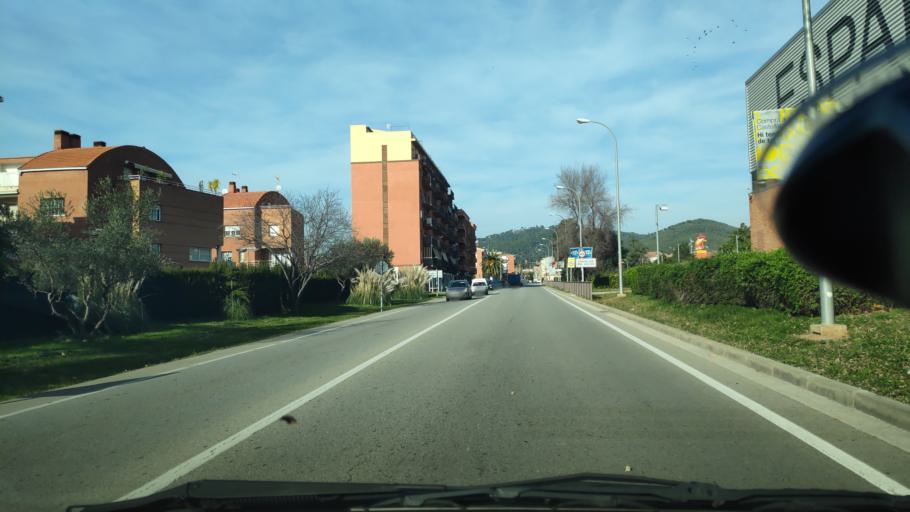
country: ES
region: Catalonia
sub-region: Provincia de Barcelona
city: Castellar del Valles
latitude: 41.6086
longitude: 2.0842
